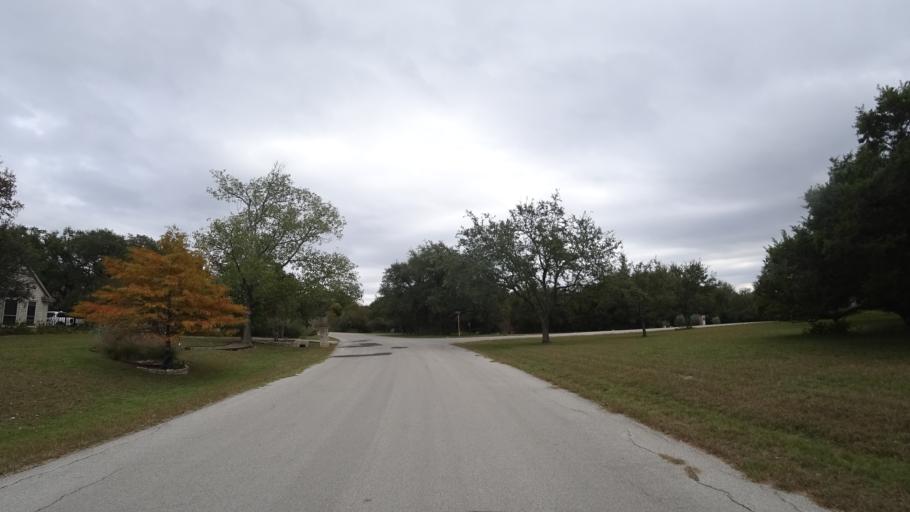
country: US
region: Texas
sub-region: Travis County
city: Shady Hollow
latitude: 30.1516
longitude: -97.8650
